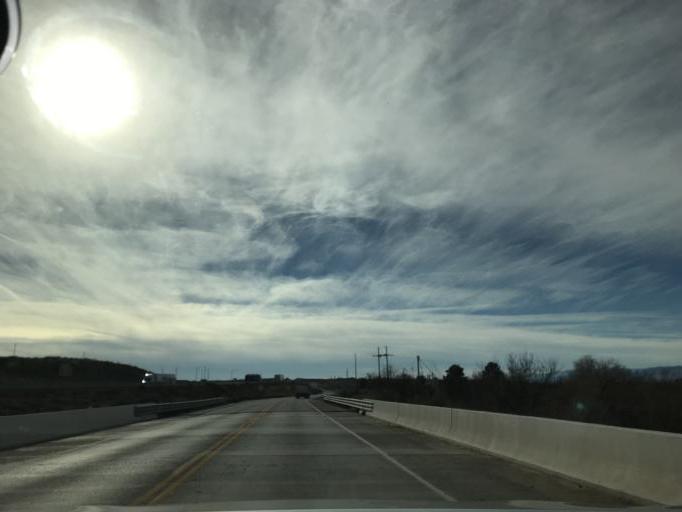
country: US
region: Nevada
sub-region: Clark County
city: Moapa Town
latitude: 36.6635
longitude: -114.5713
